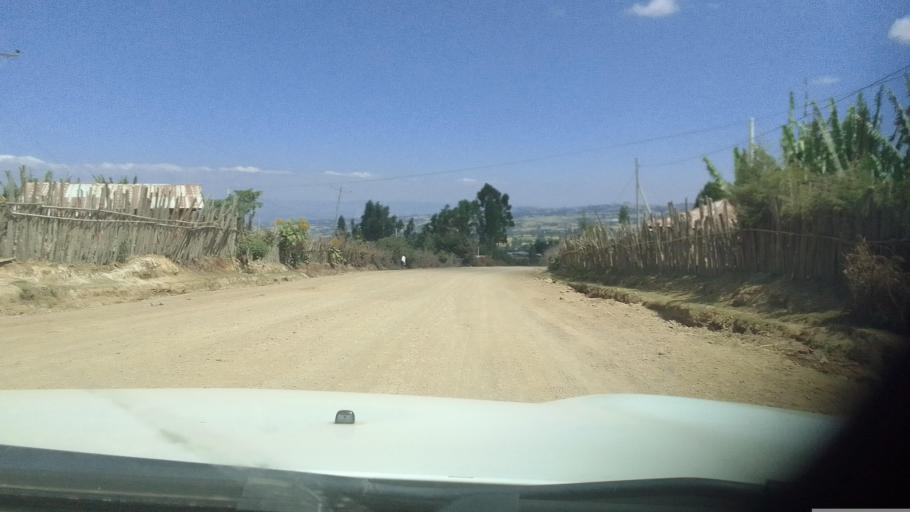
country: ET
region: Oromiya
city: Hagere Hiywet
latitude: 8.8488
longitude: 37.8889
